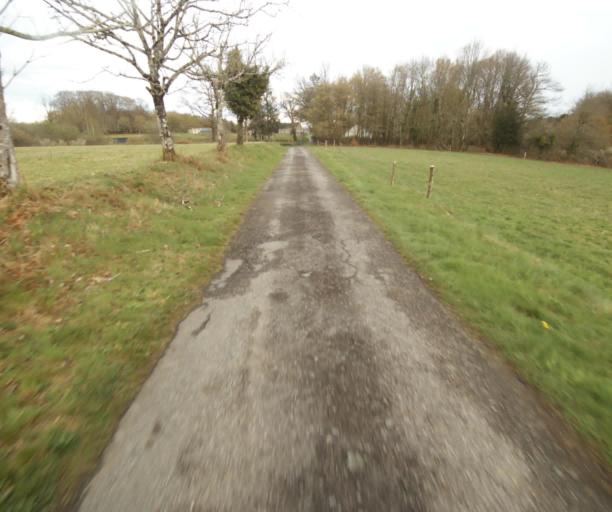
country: FR
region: Limousin
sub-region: Departement de la Correze
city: Saint-Privat
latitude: 45.2181
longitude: 2.0159
